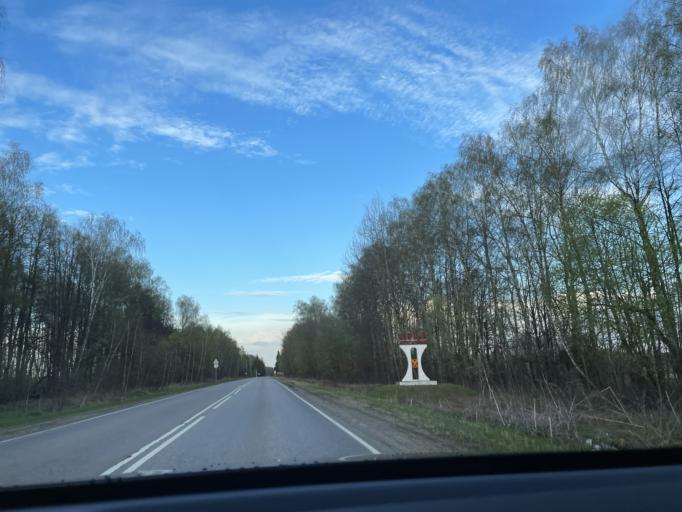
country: RU
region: Tula
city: Novogurovskiy
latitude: 54.5197
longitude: 37.2256
